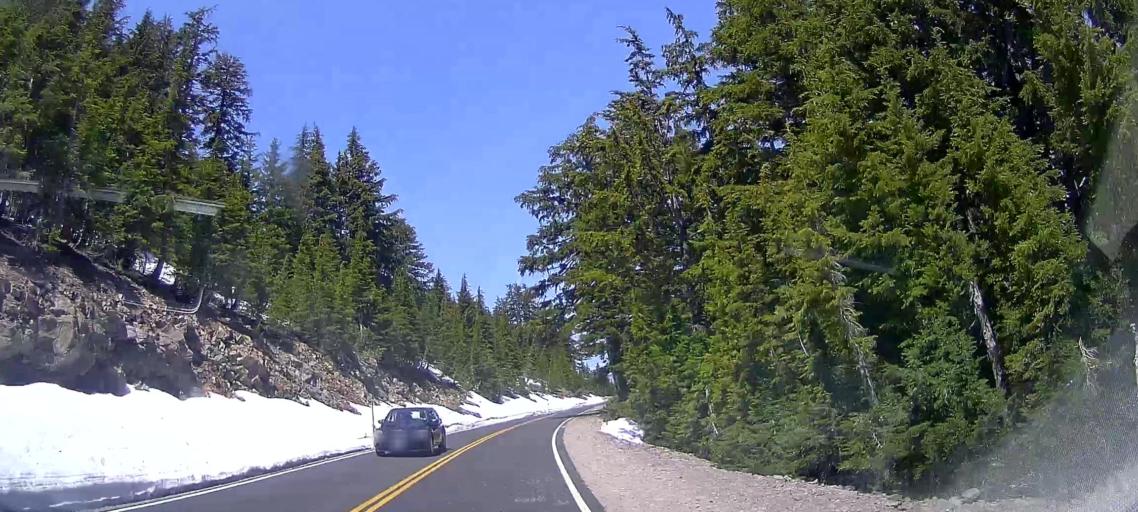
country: US
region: Oregon
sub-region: Jackson County
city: Shady Cove
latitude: 42.9807
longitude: -122.1287
